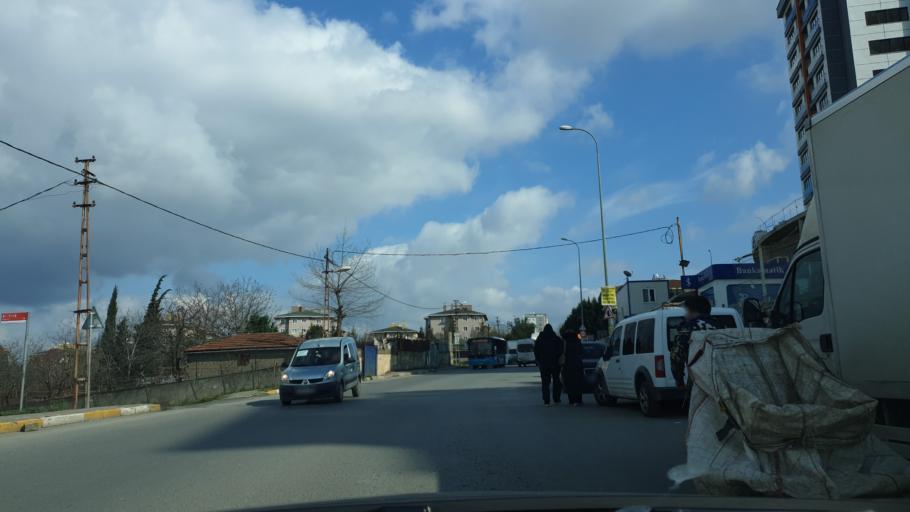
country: TR
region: Istanbul
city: Icmeler
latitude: 40.8693
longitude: 29.3160
